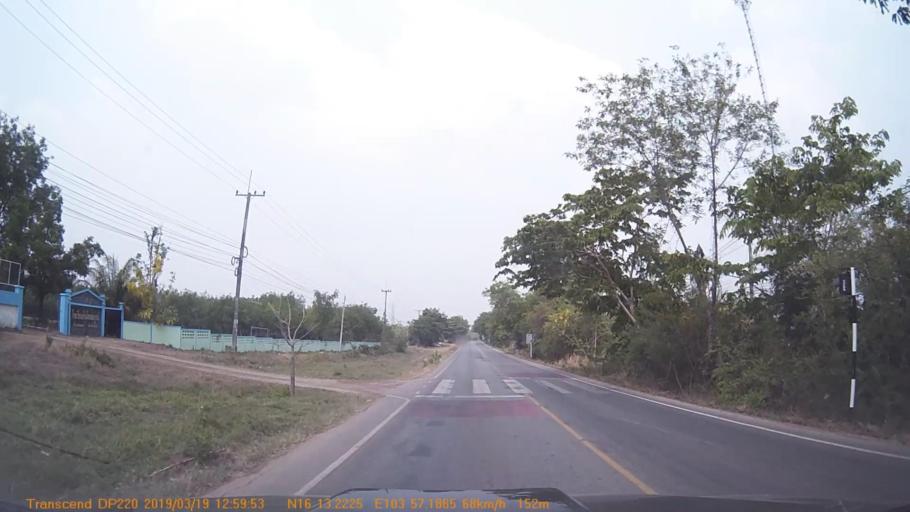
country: TH
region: Roi Et
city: Waeng
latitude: 16.2207
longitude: 103.9532
